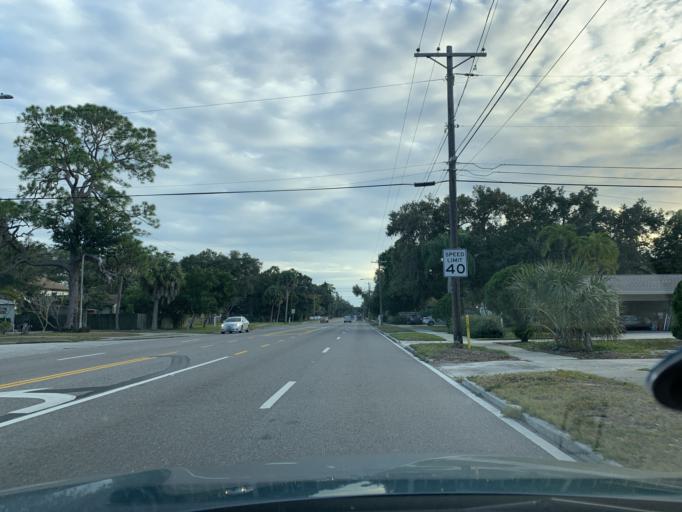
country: US
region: Florida
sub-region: Pinellas County
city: Bay Pines
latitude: 27.8036
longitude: -82.7539
